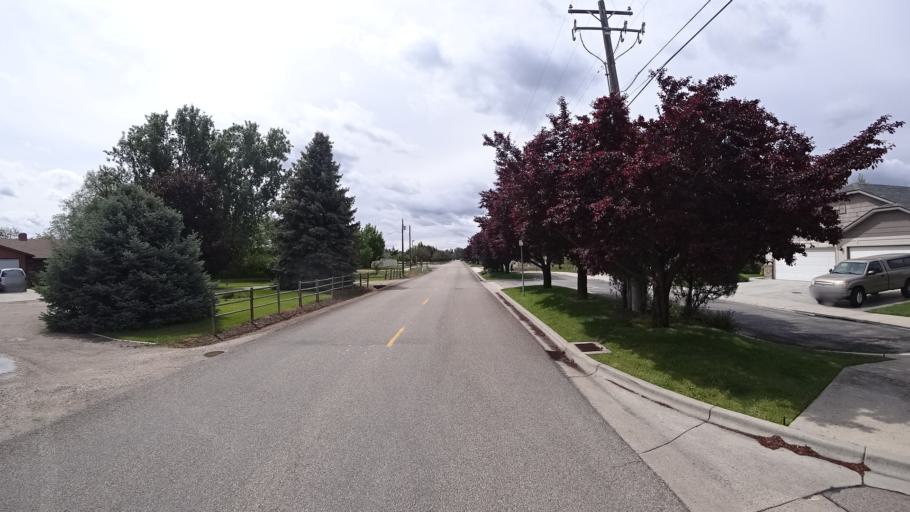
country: US
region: Idaho
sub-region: Ada County
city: Eagle
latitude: 43.6855
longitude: -116.3015
